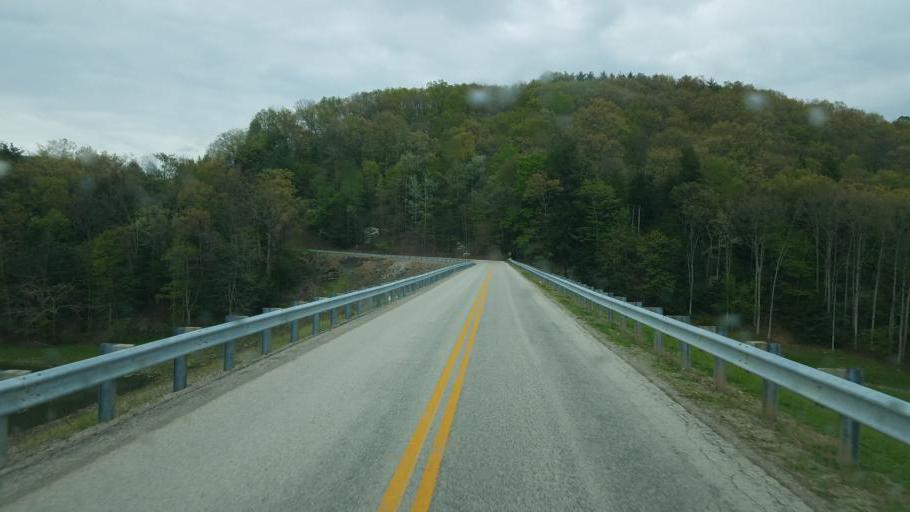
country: US
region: Ohio
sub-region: Ashland County
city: Loudonville
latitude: 40.6229
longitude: -82.3250
